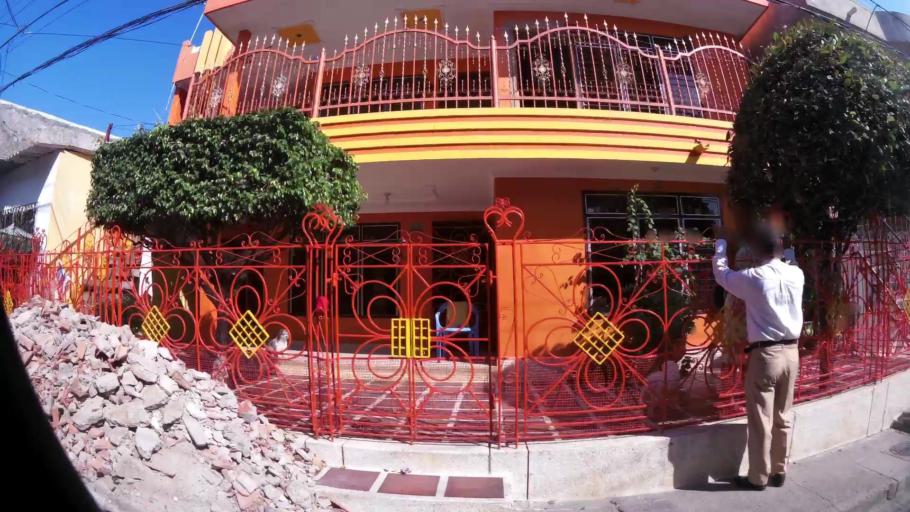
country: CO
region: Bolivar
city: Cartagena
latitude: 10.3948
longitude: -75.5007
